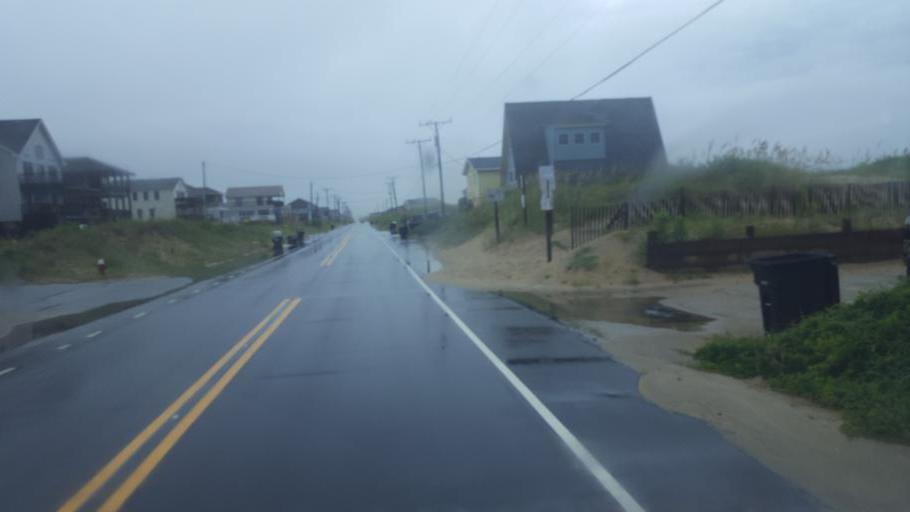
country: US
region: North Carolina
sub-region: Dare County
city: Kill Devil Hills
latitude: 36.0492
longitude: -75.6787
